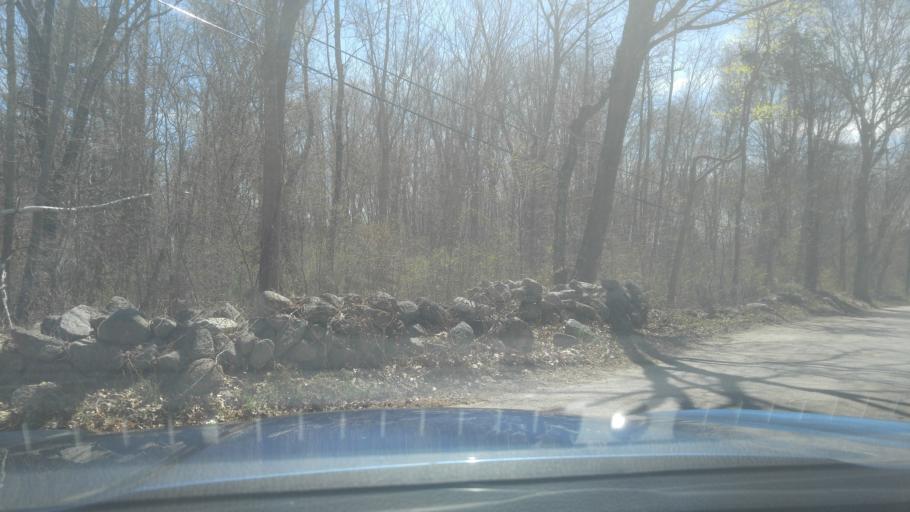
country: US
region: Rhode Island
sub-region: Washington County
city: Hope Valley
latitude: 41.5904
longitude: -71.7587
